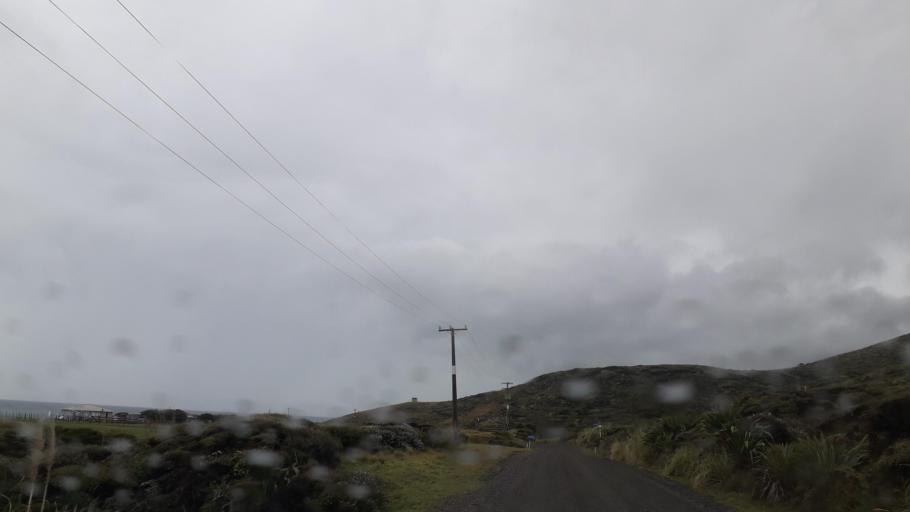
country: NZ
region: Northland
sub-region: Far North District
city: Ahipara
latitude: -35.4318
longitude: 173.2784
